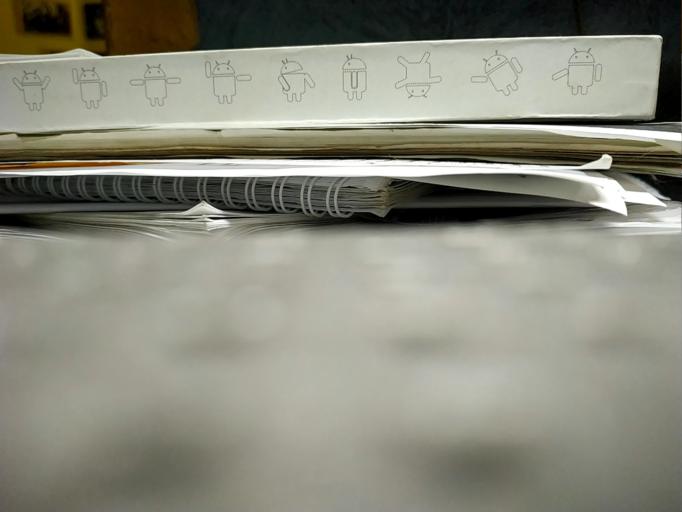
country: EE
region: Ida-Virumaa
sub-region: Narva-Joesuu linn
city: Narva-Joesuu
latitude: 59.6609
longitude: 27.9380
